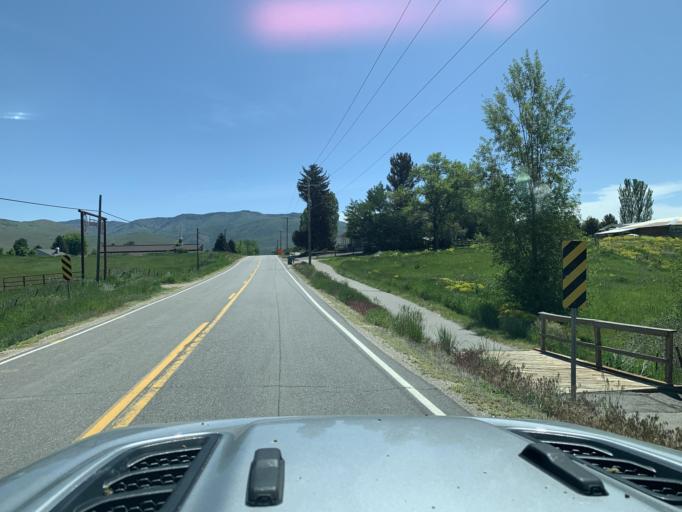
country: US
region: Utah
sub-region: Weber County
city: Wolf Creek
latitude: 41.2933
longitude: -111.7973
